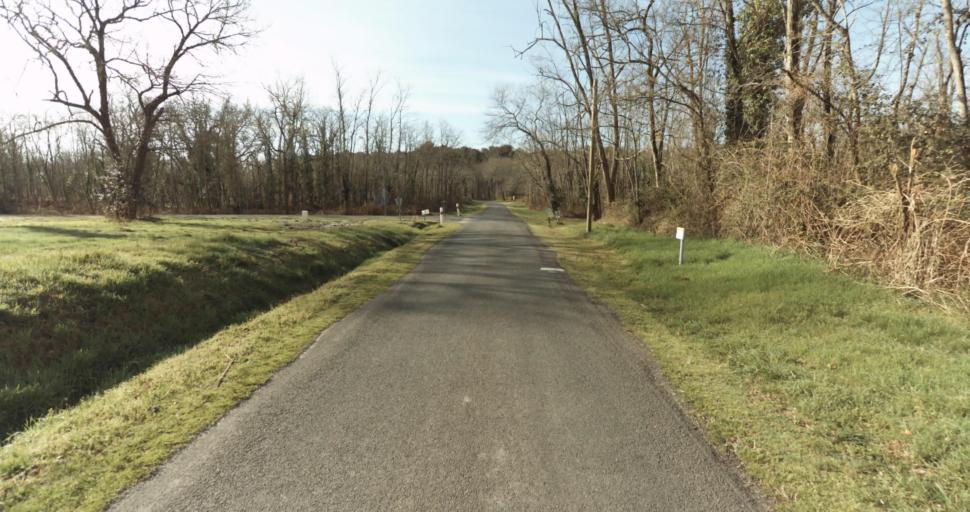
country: FR
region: Aquitaine
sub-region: Departement des Landes
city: Sarbazan
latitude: 44.0441
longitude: -0.2421
